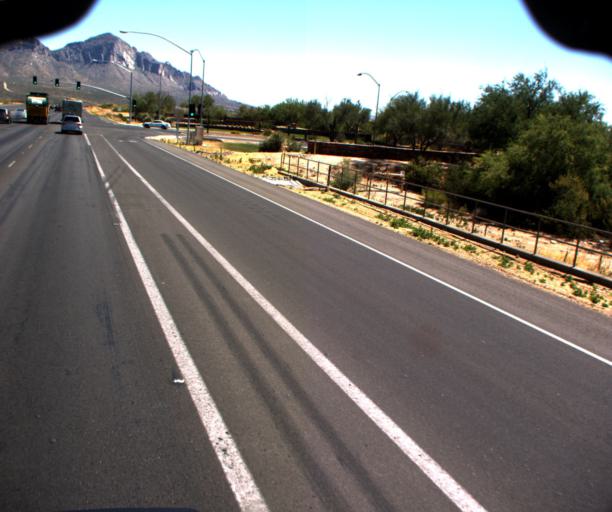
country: US
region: Arizona
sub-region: Pima County
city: Oro Valley
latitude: 32.4412
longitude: -110.9341
